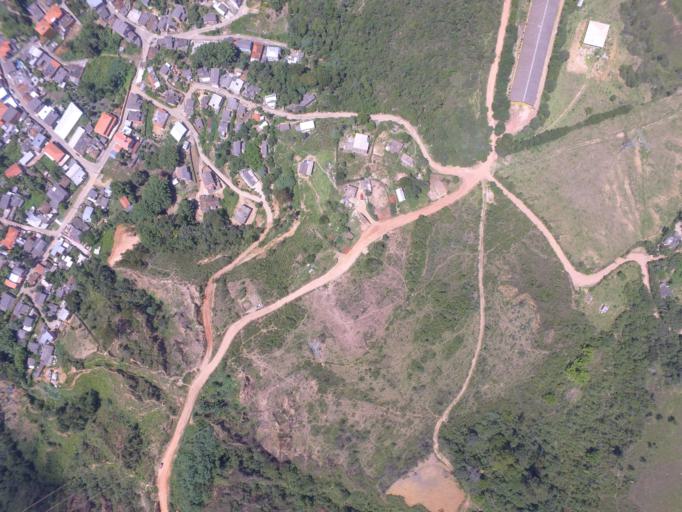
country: BR
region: Minas Gerais
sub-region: Tiradentes
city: Tiradentes
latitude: -21.0505
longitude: -44.0754
